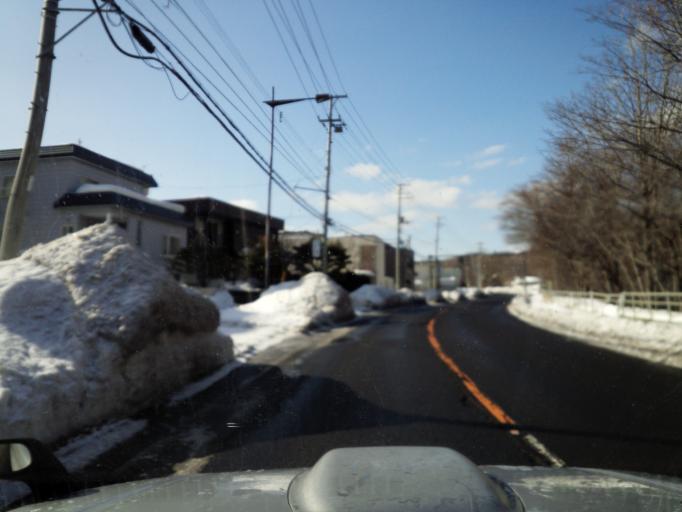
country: JP
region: Hokkaido
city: Sapporo
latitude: 42.9395
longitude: 141.3444
